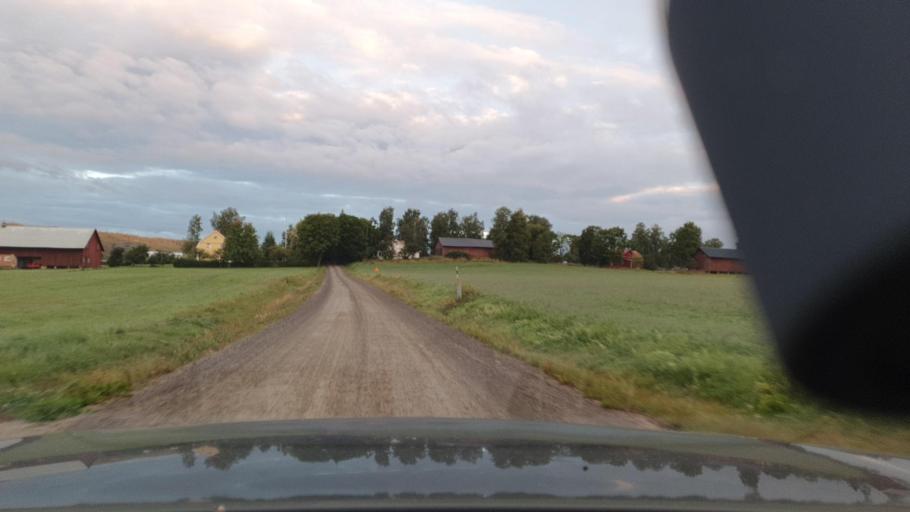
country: SE
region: Vaermland
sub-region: Sunne Kommun
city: Sunne
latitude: 59.8117
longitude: 13.0614
